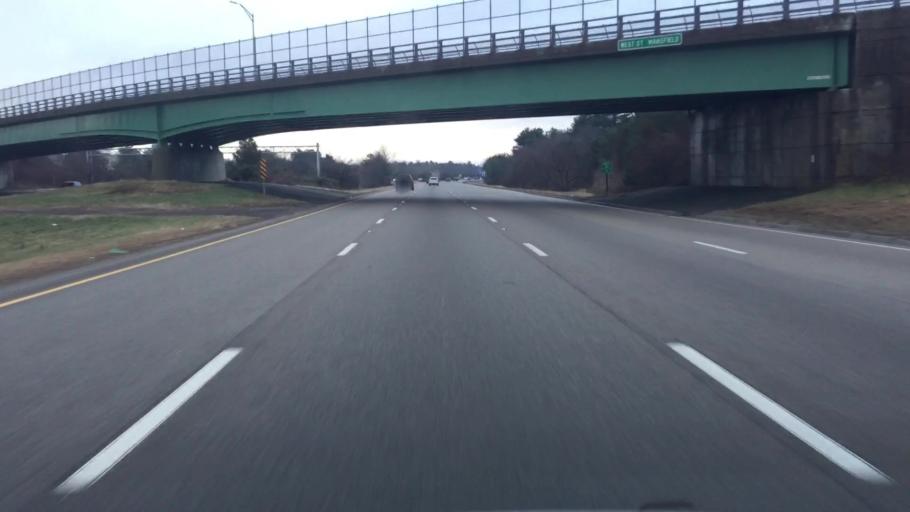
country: US
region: Massachusetts
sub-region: Bristol County
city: Mansfield
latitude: 42.0255
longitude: -71.2538
